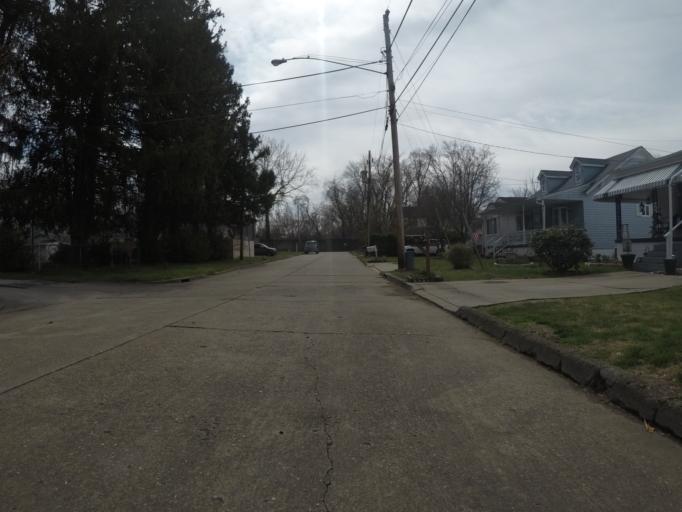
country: US
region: West Virginia
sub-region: Cabell County
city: Pea Ridge
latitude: 38.4142
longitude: -82.3662
